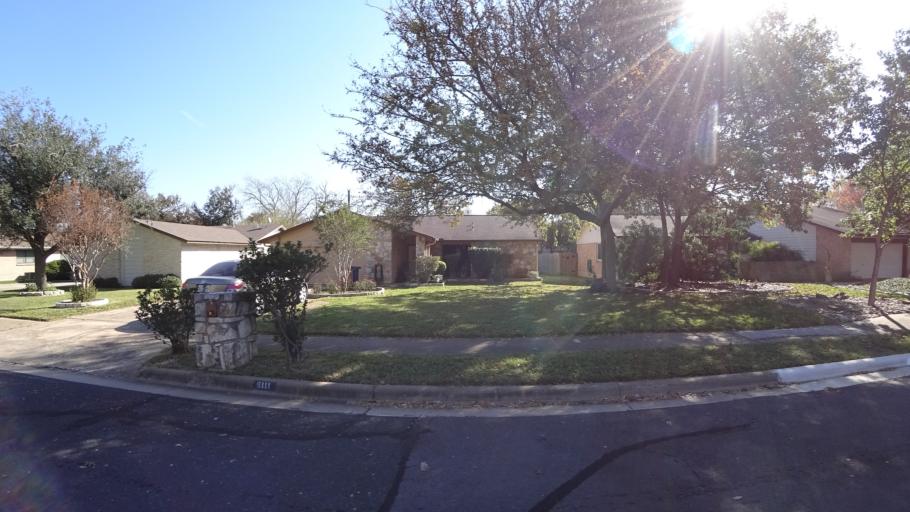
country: US
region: Texas
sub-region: Travis County
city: Barton Creek
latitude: 30.2314
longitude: -97.8482
